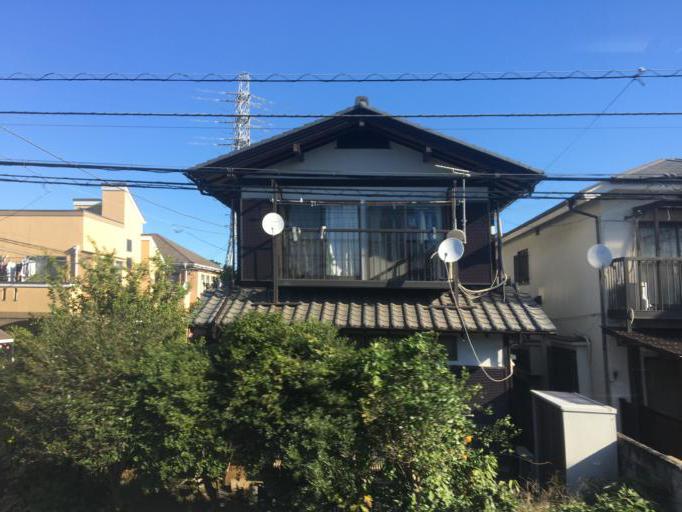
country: JP
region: Chiba
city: Funabashi
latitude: 35.7106
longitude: 139.9647
